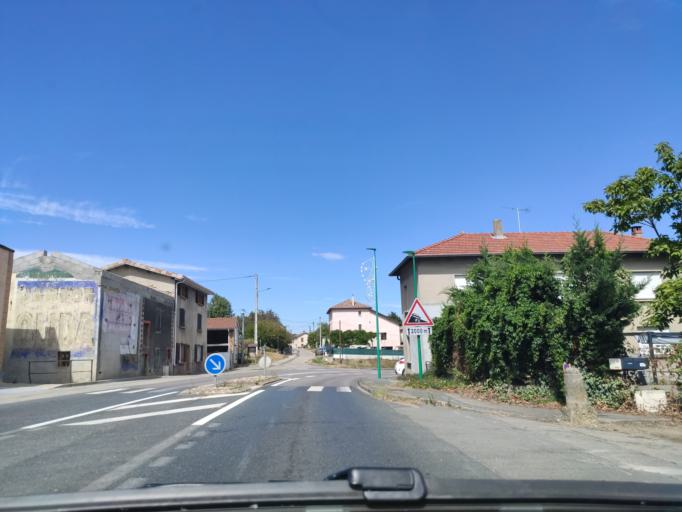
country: FR
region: Rhone-Alpes
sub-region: Departement de l'Isere
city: Reventin-Vaugris
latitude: 45.4787
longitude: 4.8295
